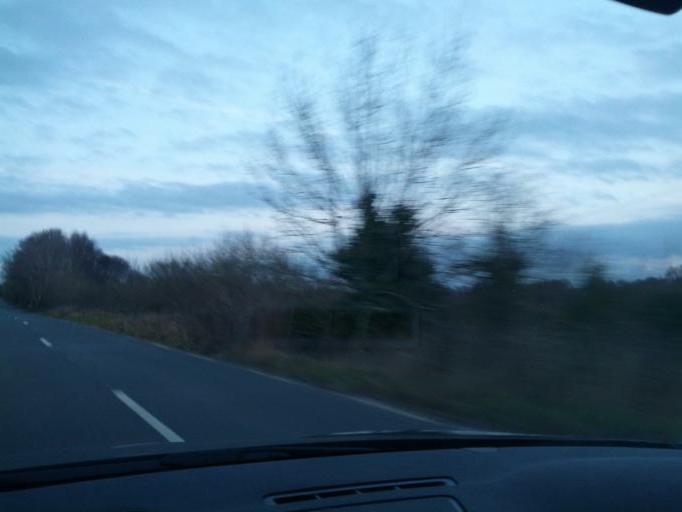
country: IE
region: Connaught
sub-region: County Galway
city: Portumna
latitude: 53.0558
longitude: -8.0986
